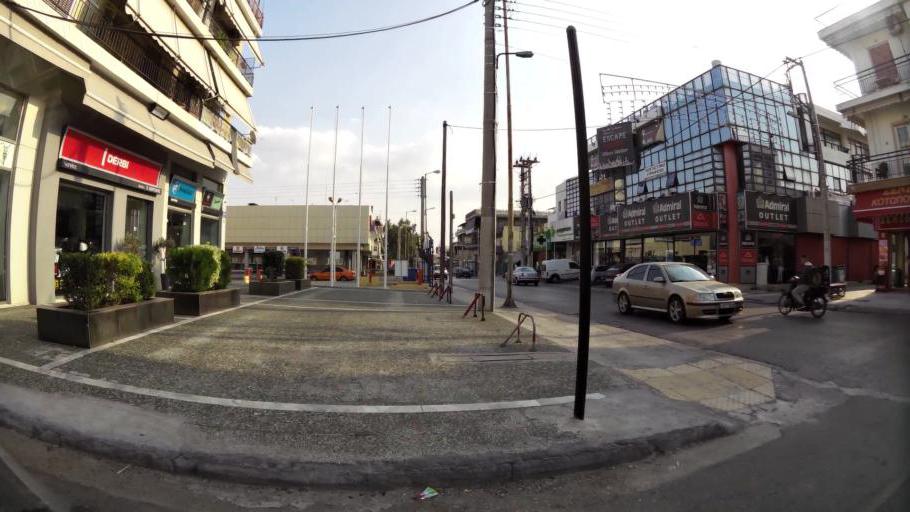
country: GR
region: Attica
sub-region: Nomarchia Athinas
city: Ilion
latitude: 38.0310
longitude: 23.6974
